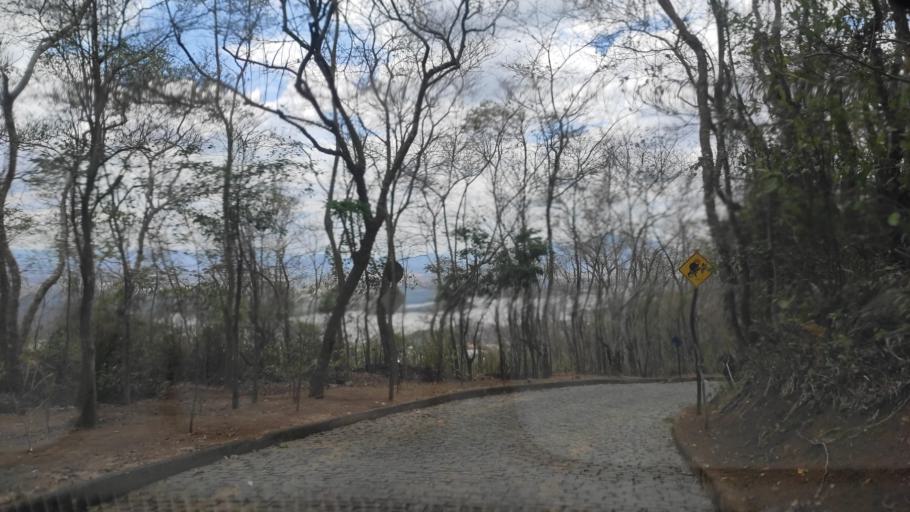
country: BR
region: Espirito Santo
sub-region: Vitoria
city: Vitoria
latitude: -20.3082
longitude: -40.3417
